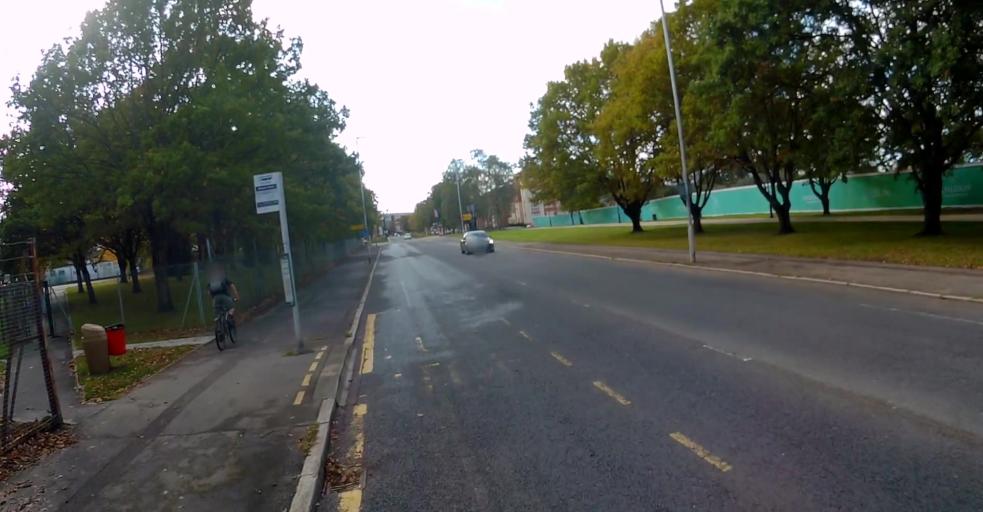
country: GB
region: England
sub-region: Hampshire
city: Aldershot
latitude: 51.2579
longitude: -0.7625
